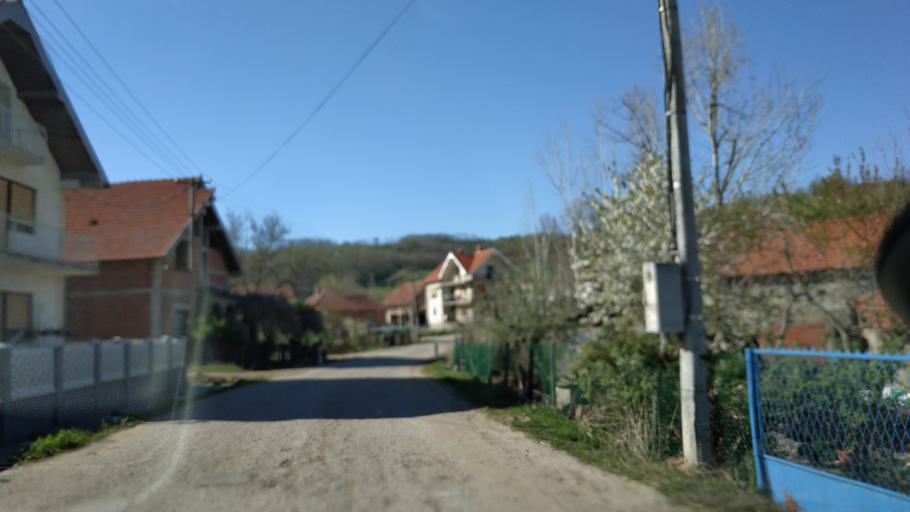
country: RS
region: Central Serbia
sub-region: Nisavski Okrug
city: Aleksinac
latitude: 43.4748
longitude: 21.6450
